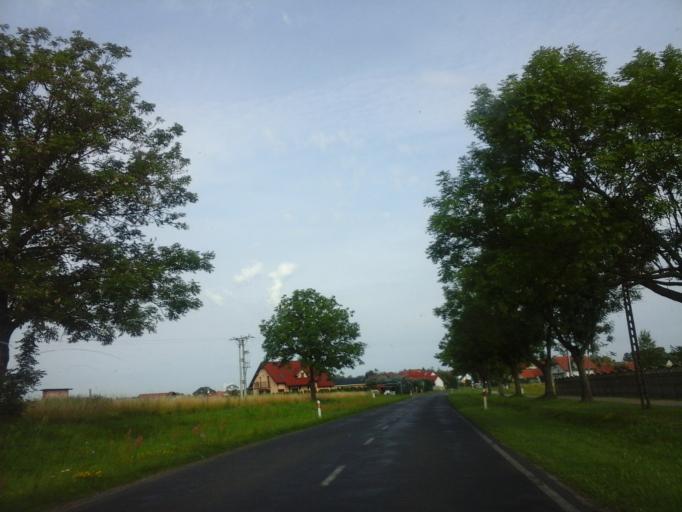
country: PL
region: West Pomeranian Voivodeship
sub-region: Powiat stargardzki
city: Stargard Szczecinski
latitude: 53.2943
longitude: 15.0546
